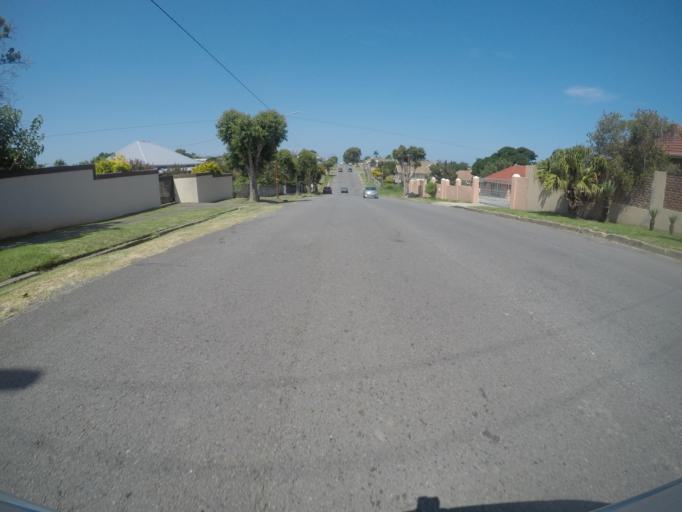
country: ZA
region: Eastern Cape
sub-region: Buffalo City Metropolitan Municipality
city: East London
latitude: -32.9808
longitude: 27.8865
